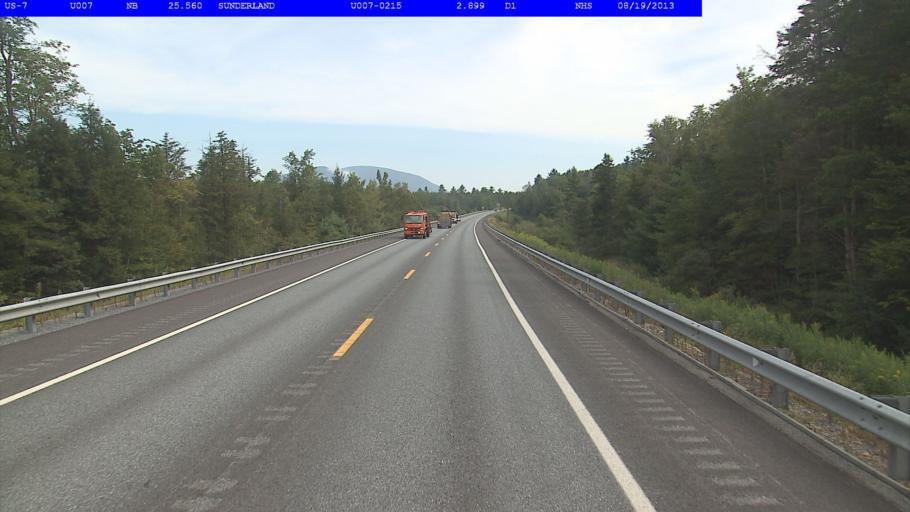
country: US
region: Vermont
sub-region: Bennington County
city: Arlington
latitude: 43.0659
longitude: -73.1237
